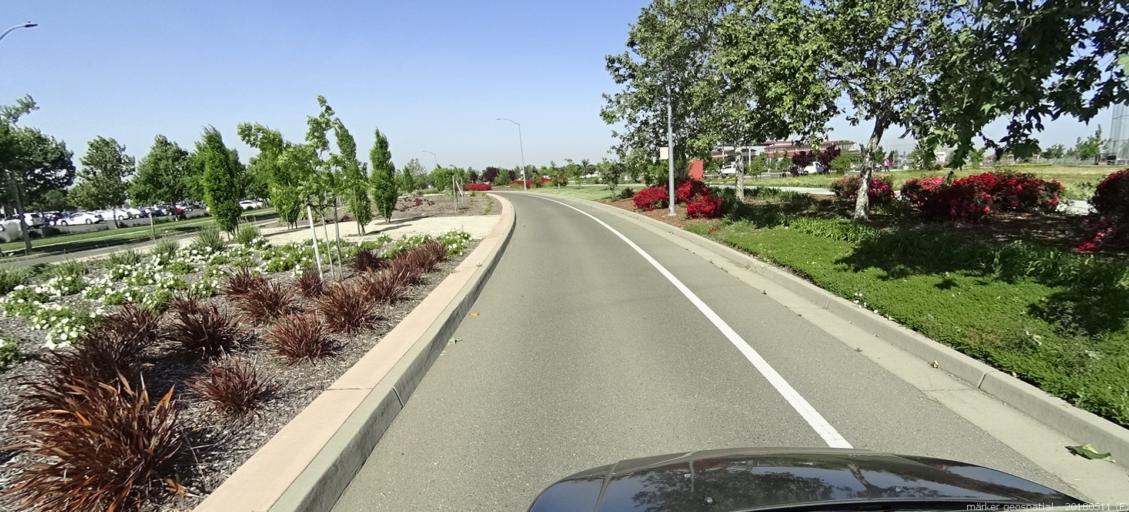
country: US
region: California
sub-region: Sacramento County
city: Rio Linda
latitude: 38.6604
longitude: -121.5161
